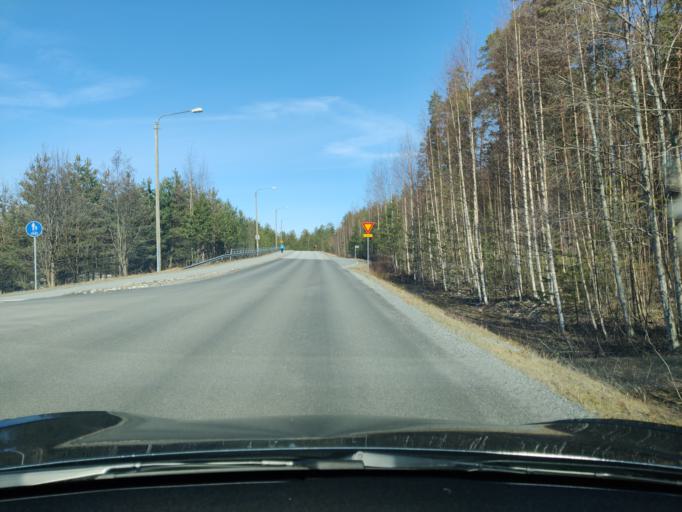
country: FI
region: Northern Savo
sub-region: Kuopio
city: Vehmersalmi
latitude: 62.7692
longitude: 28.0099
